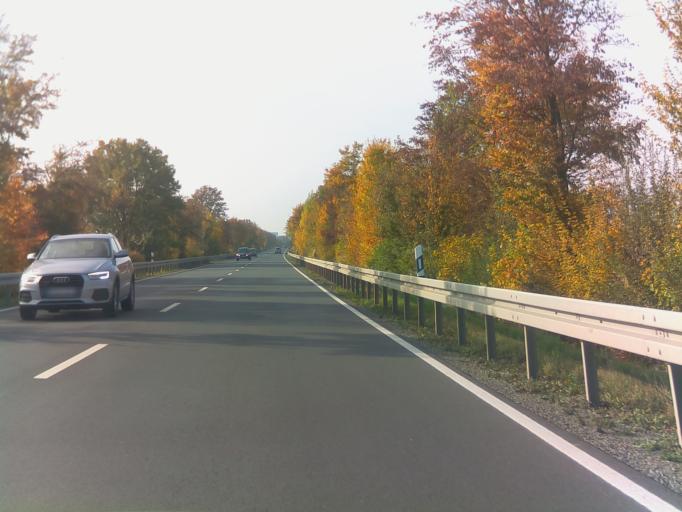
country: DE
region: Bavaria
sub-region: Regierungsbezirk Unterfranken
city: Biebelried
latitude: 49.7891
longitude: 10.1040
